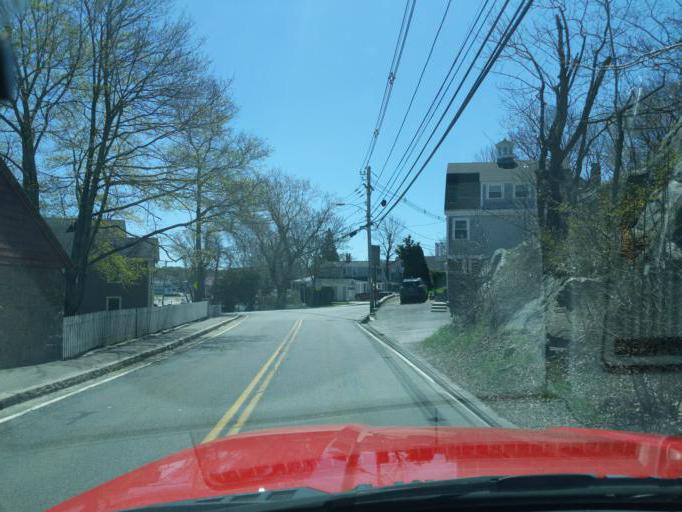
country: US
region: Massachusetts
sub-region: Essex County
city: Rockport
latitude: 42.6639
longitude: -70.6244
